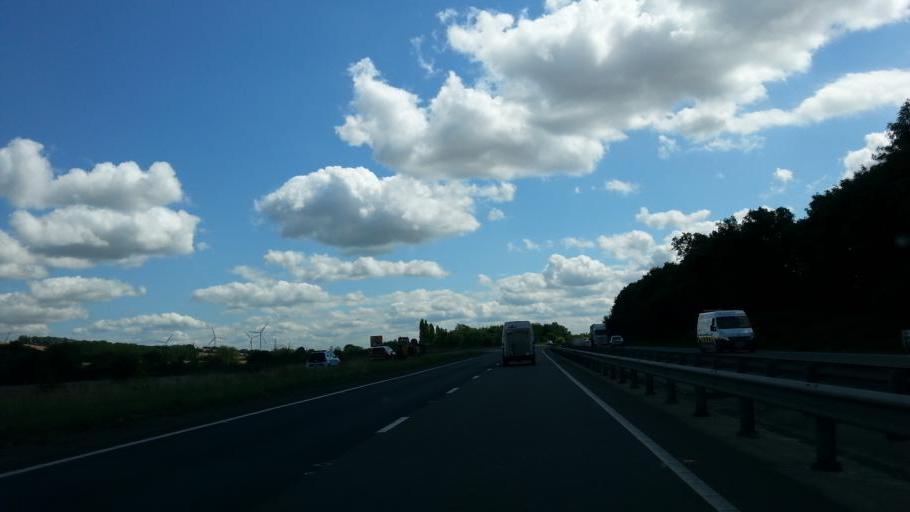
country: GB
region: England
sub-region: Bedford
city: Pertenhall
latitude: 52.3448
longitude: -0.3462
